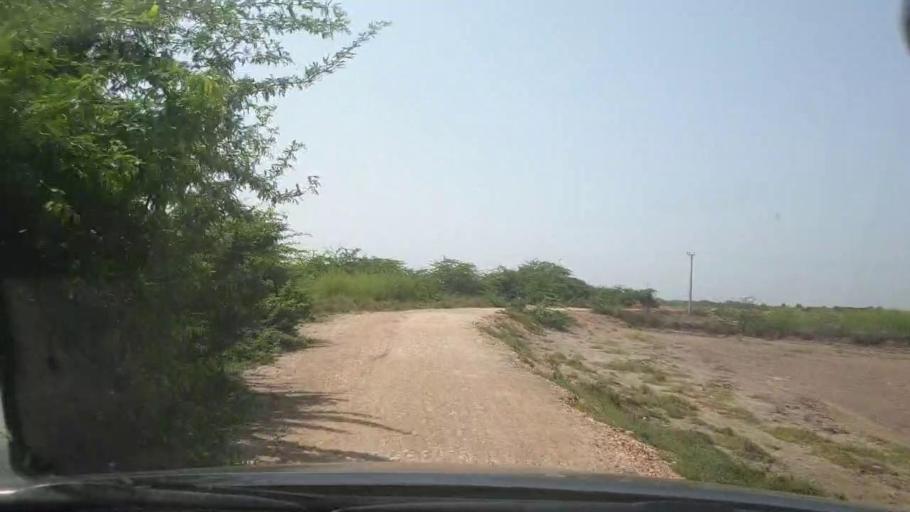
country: PK
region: Sindh
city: Tando Bago
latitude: 24.8041
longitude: 69.1554
